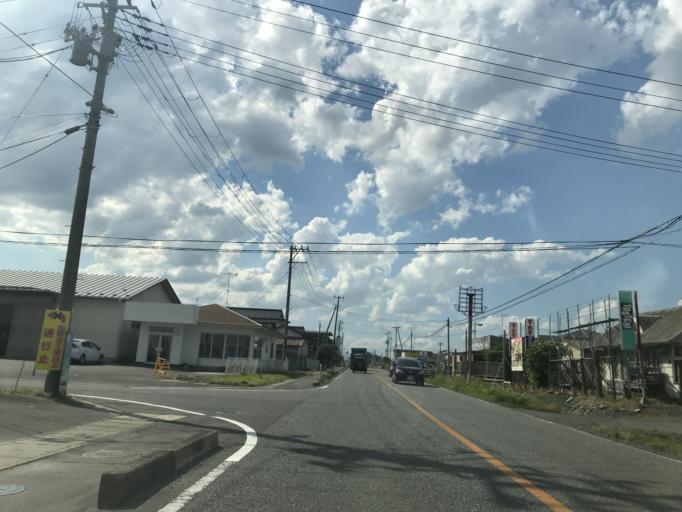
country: JP
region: Miyagi
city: Wakuya
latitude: 38.7054
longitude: 141.1837
